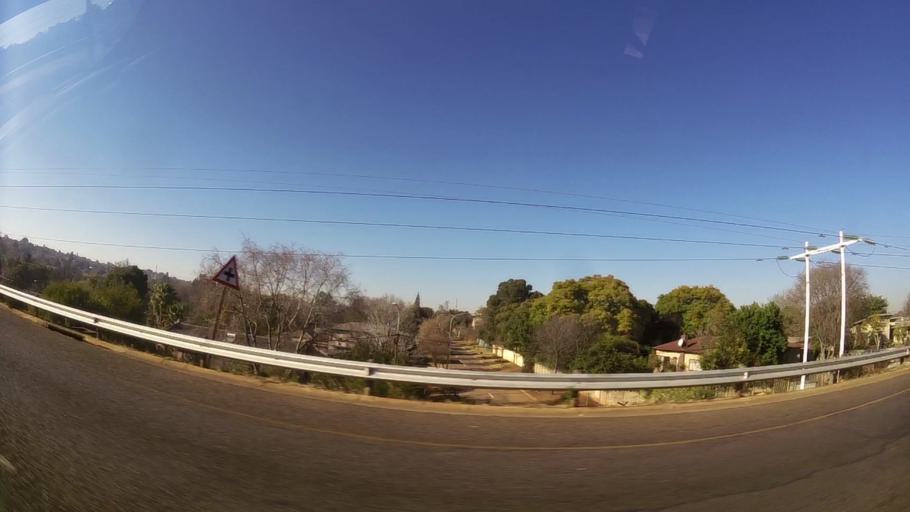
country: ZA
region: Gauteng
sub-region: City of Tshwane Metropolitan Municipality
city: Centurion
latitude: -25.8184
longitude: 28.2008
